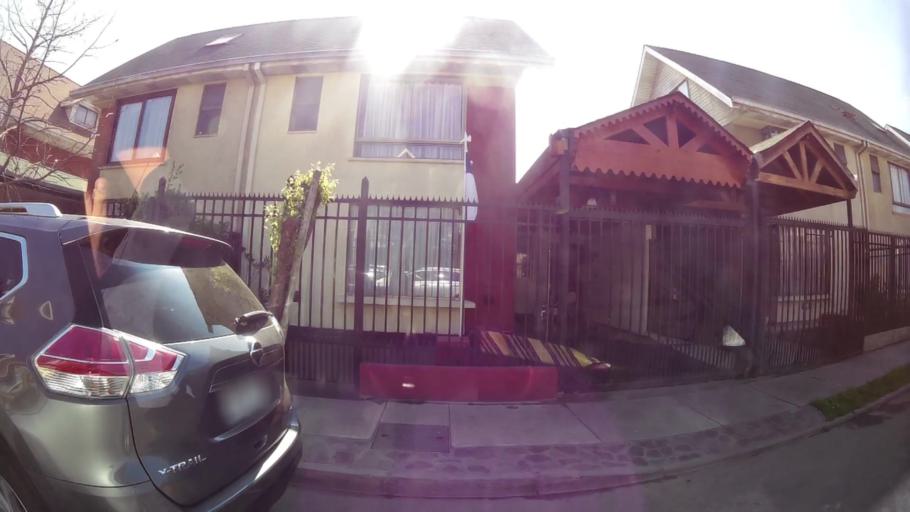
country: CL
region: Santiago Metropolitan
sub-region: Provincia de Santiago
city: Lo Prado
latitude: -33.4810
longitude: -70.7595
